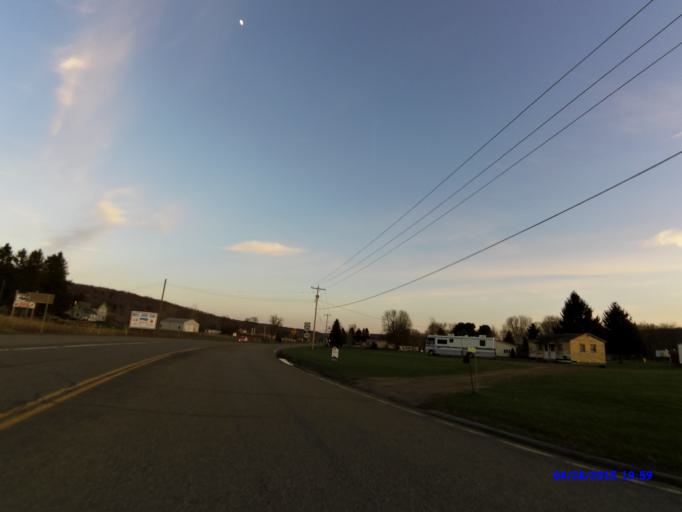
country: US
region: New York
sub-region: Cattaraugus County
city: Franklinville
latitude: 42.3656
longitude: -78.4518
